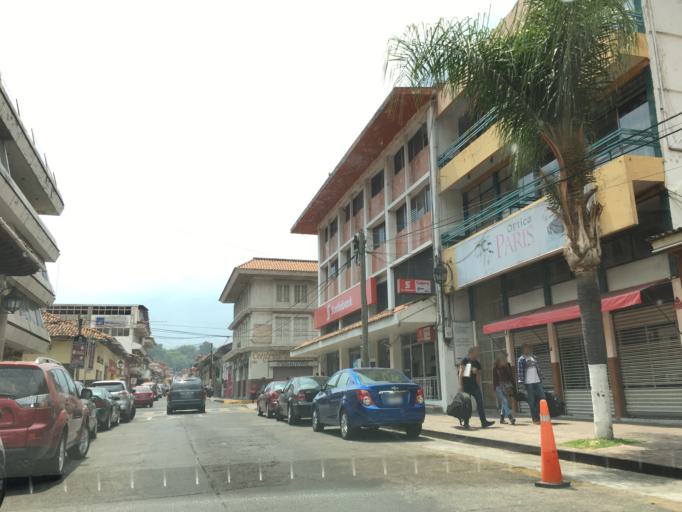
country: MX
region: Michoacan
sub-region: Uruapan
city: Uruapan
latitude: 19.4222
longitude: -102.0642
